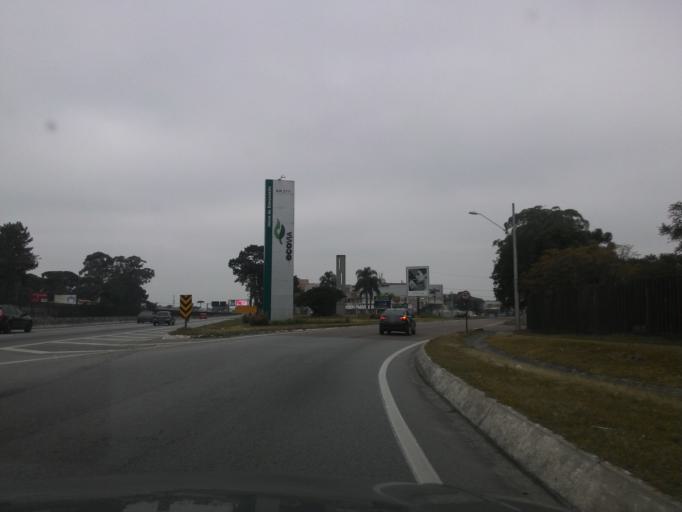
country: BR
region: Parana
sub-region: Pinhais
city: Pinhais
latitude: -25.4479
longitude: -49.2303
